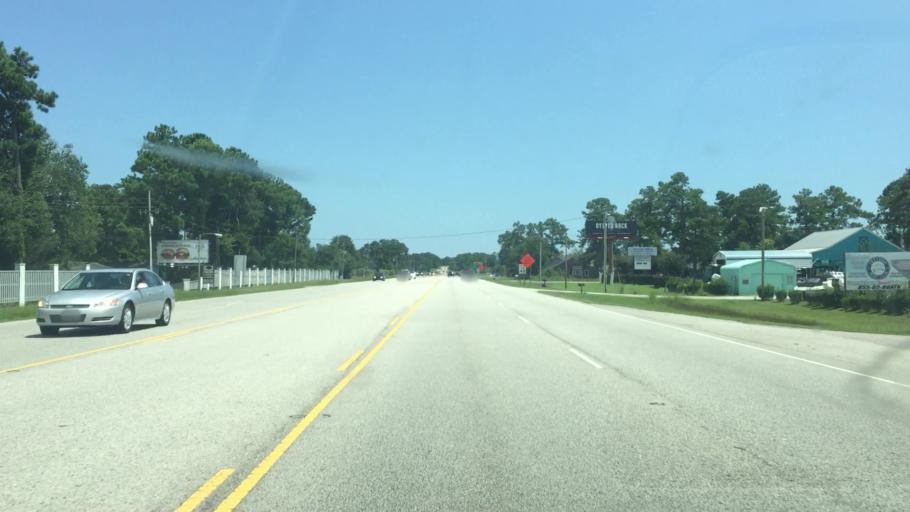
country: US
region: South Carolina
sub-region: Horry County
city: North Myrtle Beach
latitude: 33.8706
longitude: -78.6707
